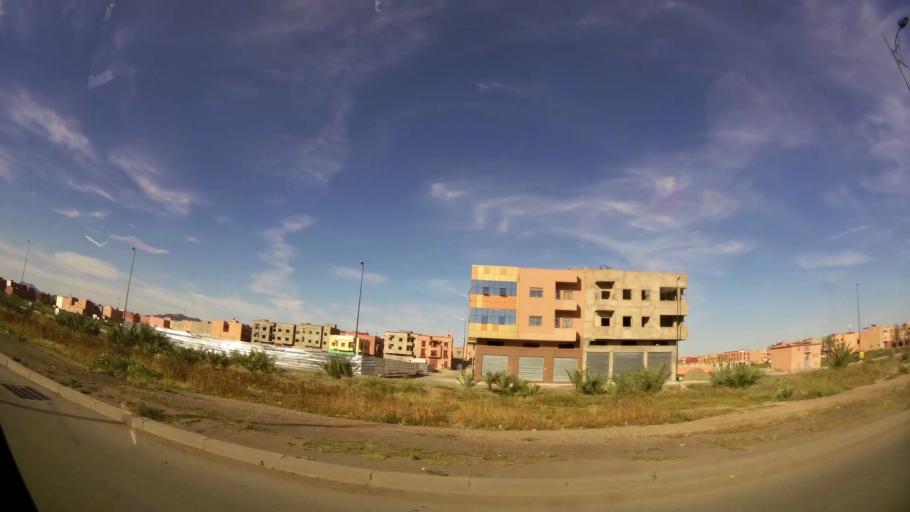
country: MA
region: Marrakech-Tensift-Al Haouz
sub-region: Marrakech
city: Marrakesh
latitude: 31.6746
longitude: -8.0440
